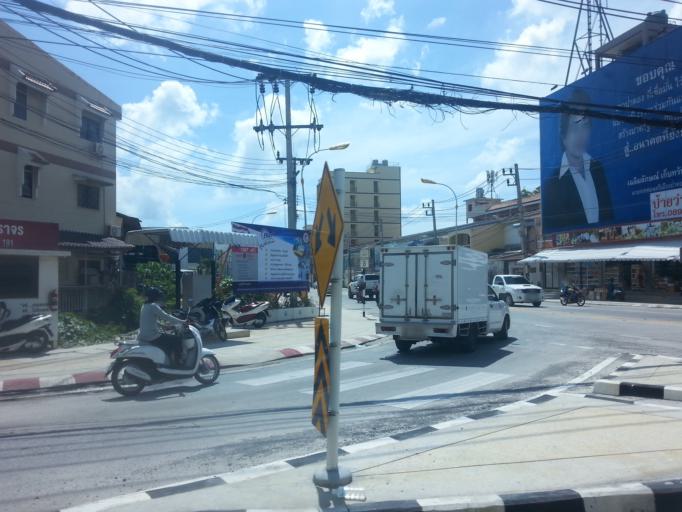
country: TH
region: Phuket
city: Patong
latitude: 7.9039
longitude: 98.3052
